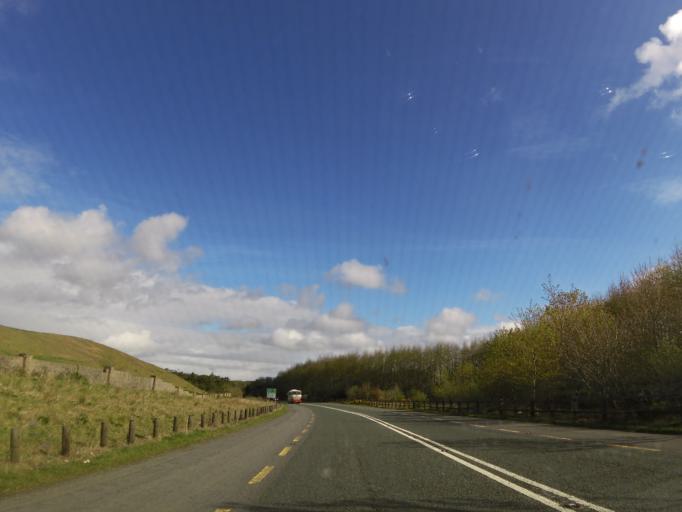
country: IE
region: Connaught
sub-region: Maigh Eo
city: Ballyhaunis
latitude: 53.8582
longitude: -8.8549
